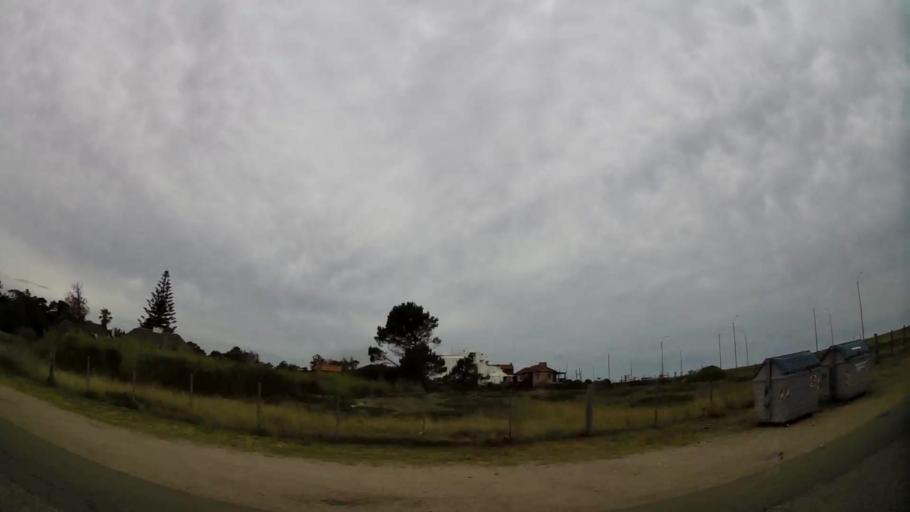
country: UY
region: Maldonado
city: Maldonado
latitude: -34.9082
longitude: -55.0041
